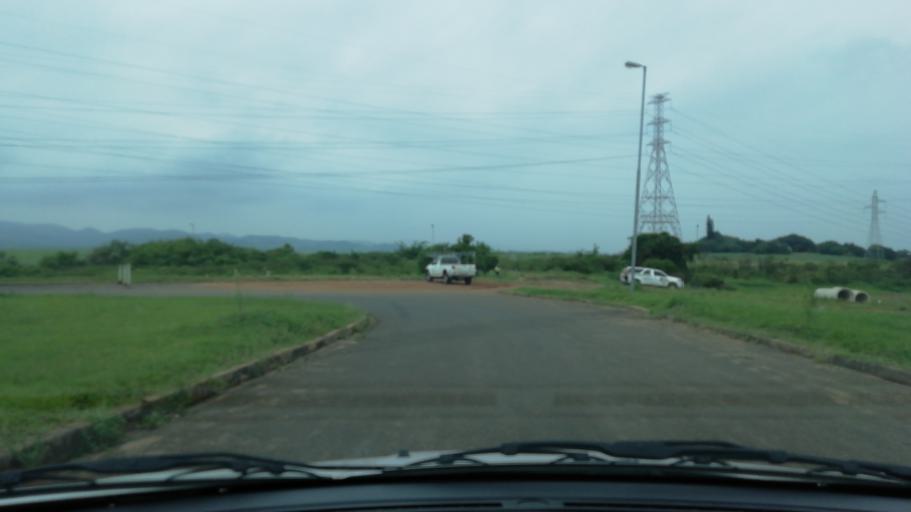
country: ZA
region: KwaZulu-Natal
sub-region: uThungulu District Municipality
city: Empangeni
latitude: -28.7368
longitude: 31.8910
